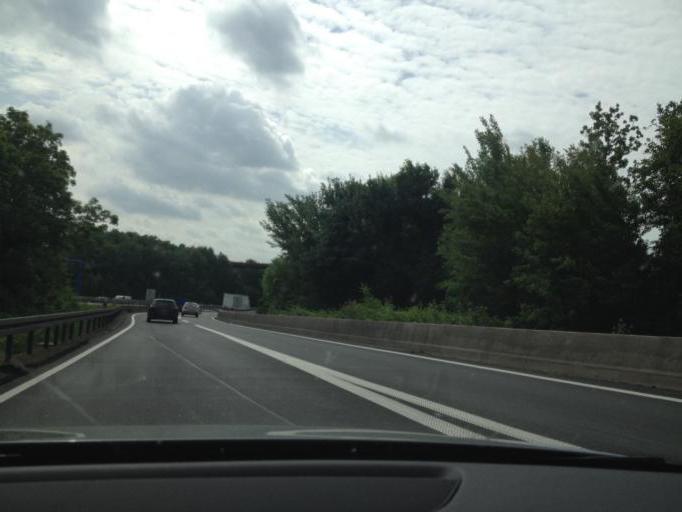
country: DE
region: North Rhine-Westphalia
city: Meiderich
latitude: 51.4827
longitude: 6.7695
